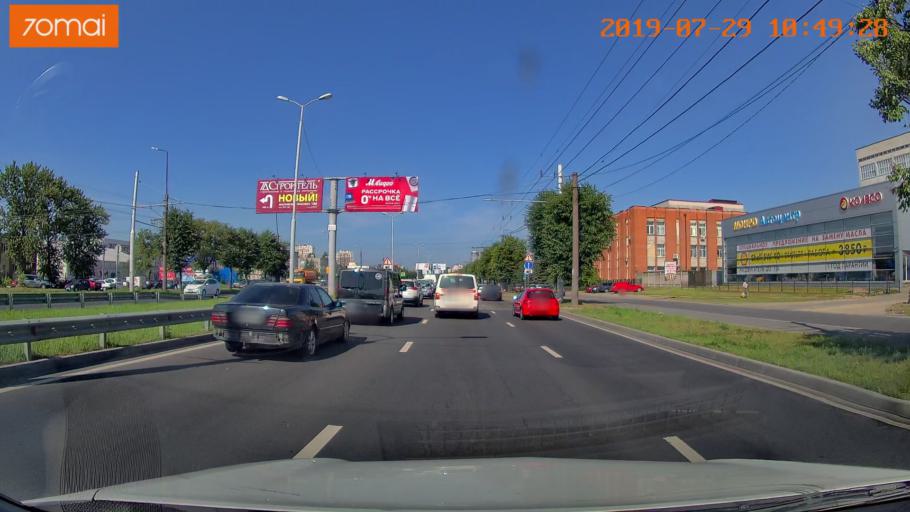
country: RU
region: Kaliningrad
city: Maloye Isakovo
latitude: 54.7094
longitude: 20.5556
